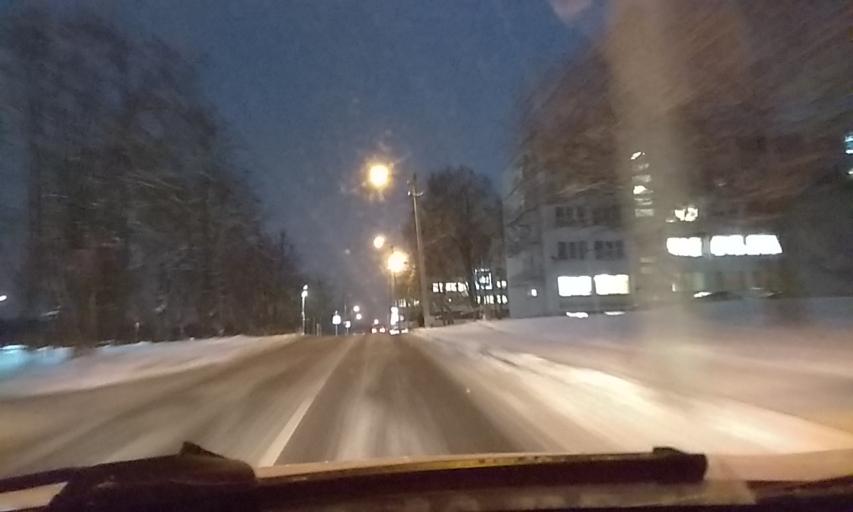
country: LT
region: Kauno apskritis
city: Dainava (Kaunas)
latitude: 54.9038
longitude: 23.9606
